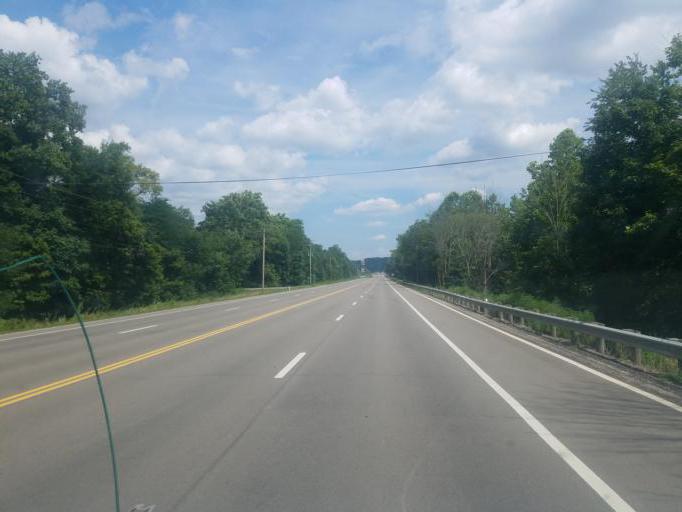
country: US
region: Ohio
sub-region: Muskingum County
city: Zanesville
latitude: 39.9523
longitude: -82.0597
